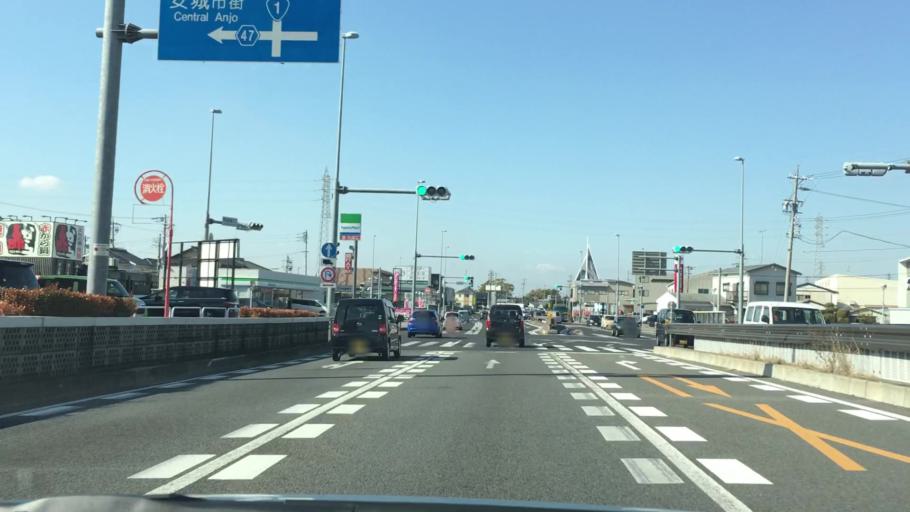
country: JP
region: Aichi
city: Okazaki
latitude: 34.9647
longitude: 137.1371
